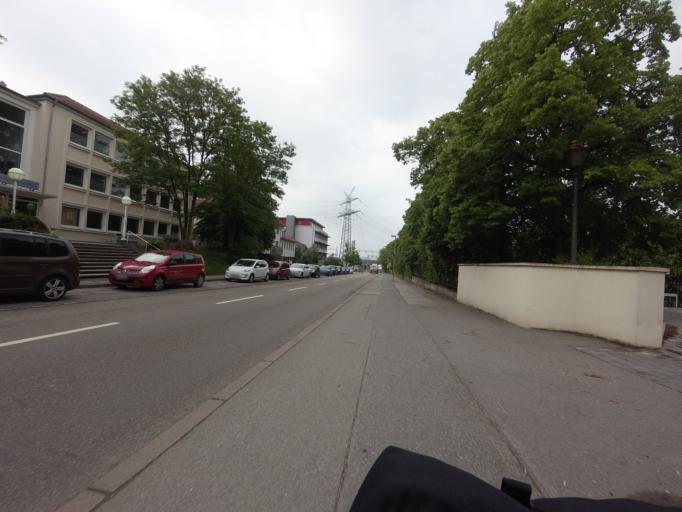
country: DE
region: Mecklenburg-Vorpommern
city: Selmsdorf
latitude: 53.9010
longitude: 10.8023
